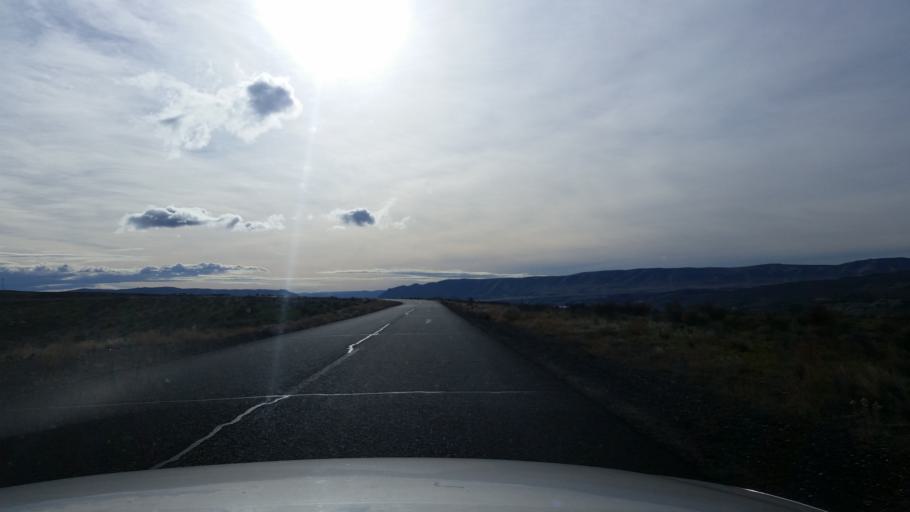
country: US
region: Washington
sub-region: Grant County
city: Mattawa
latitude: 46.9678
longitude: -119.9667
